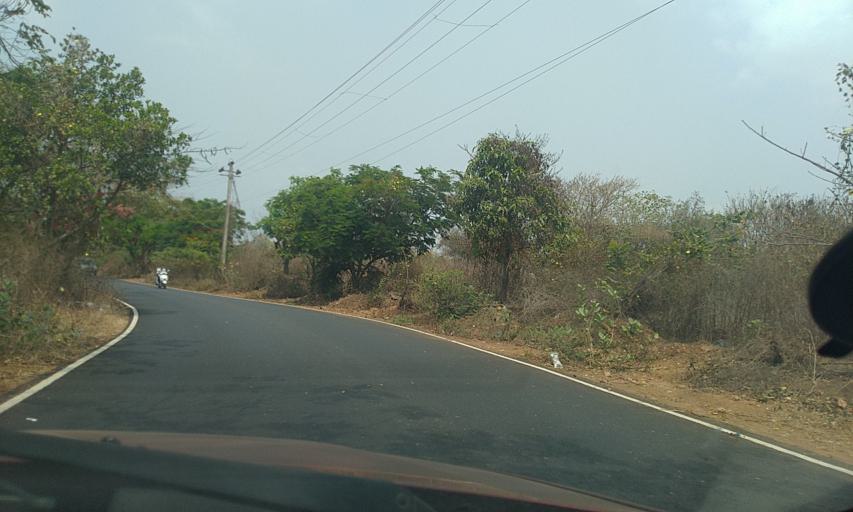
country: IN
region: Goa
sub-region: North Goa
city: Mapuca
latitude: 15.6081
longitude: 73.8000
